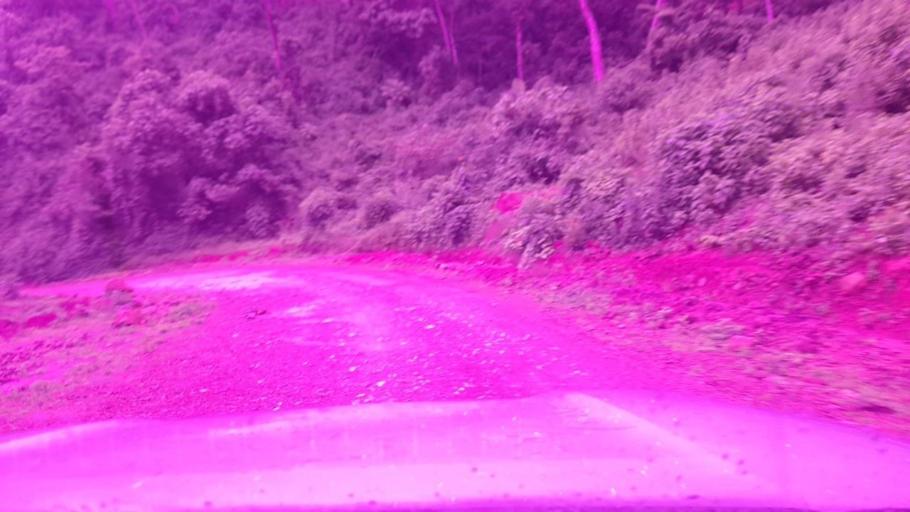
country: ET
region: Southern Nations, Nationalities, and People's Region
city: Bonga
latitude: 7.5124
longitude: 36.0571
